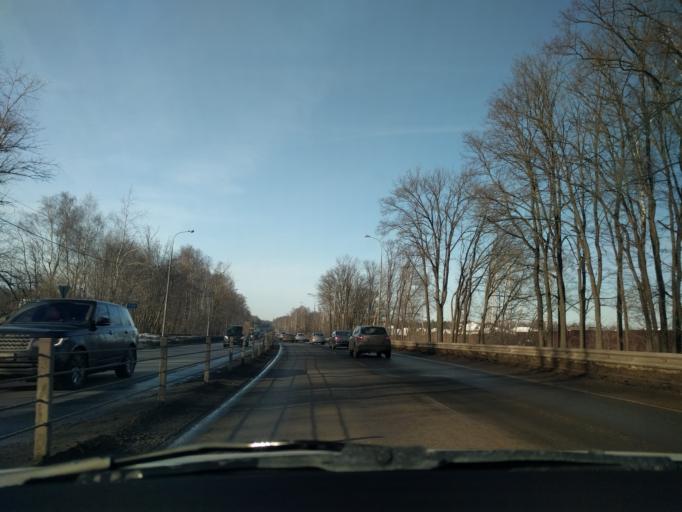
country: RU
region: Moskovskaya
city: Marfino
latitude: 56.0144
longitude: 37.5464
